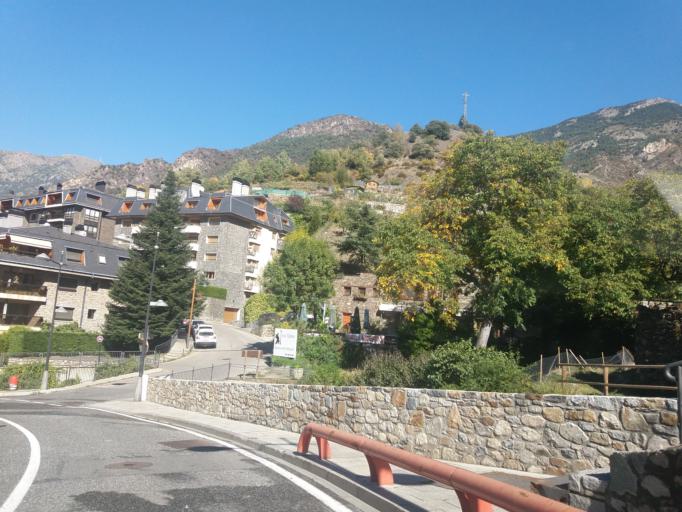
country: AD
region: Sant Julia de Loria
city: Sant Julia de Loria
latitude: 42.4654
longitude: 1.4947
